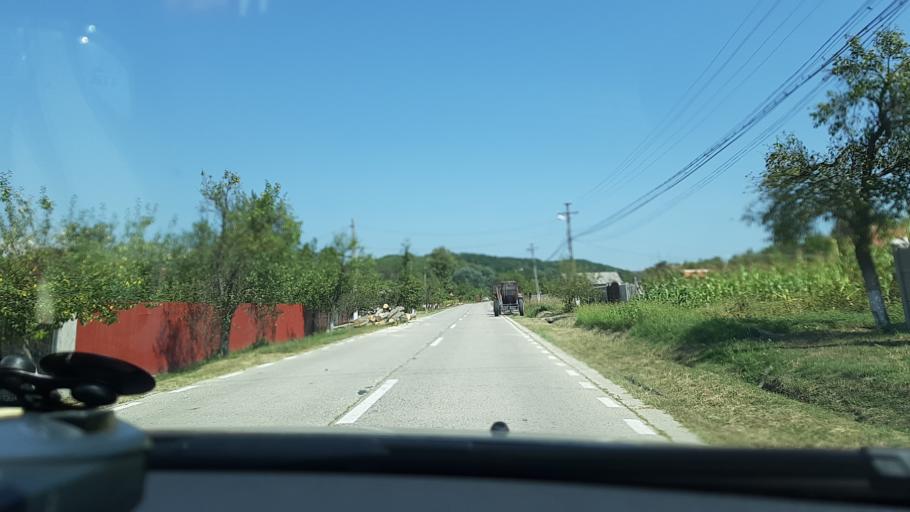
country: RO
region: Gorj
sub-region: Comuna Logresti-Mosteni
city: Logresti Mosteni
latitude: 44.8967
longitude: 23.7309
